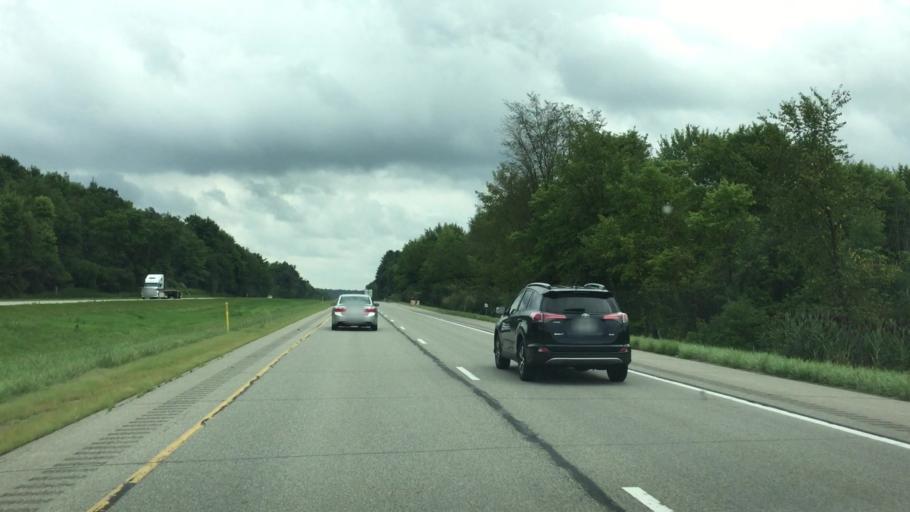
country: US
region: Pennsylvania
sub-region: Butler County
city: Slippery Rock
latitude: 41.0870
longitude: -80.1370
